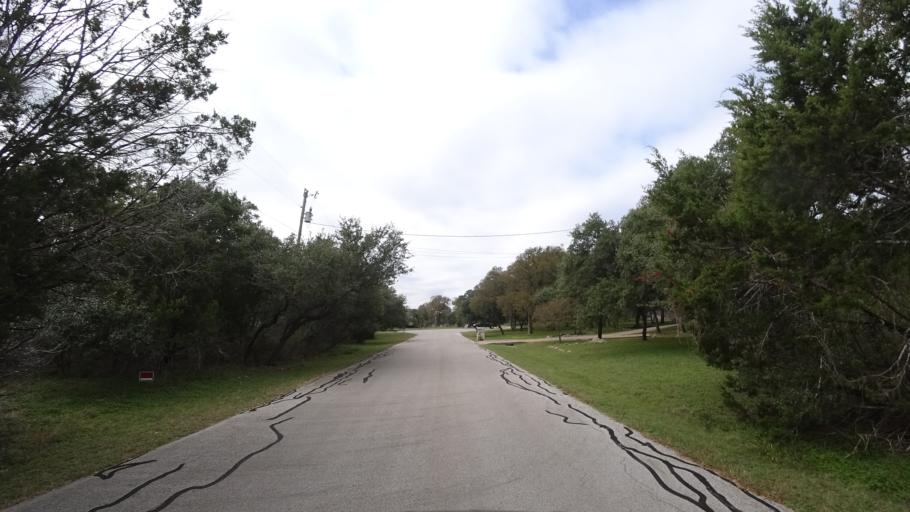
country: US
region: Texas
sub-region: Travis County
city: Shady Hollow
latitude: 30.1346
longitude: -97.8837
